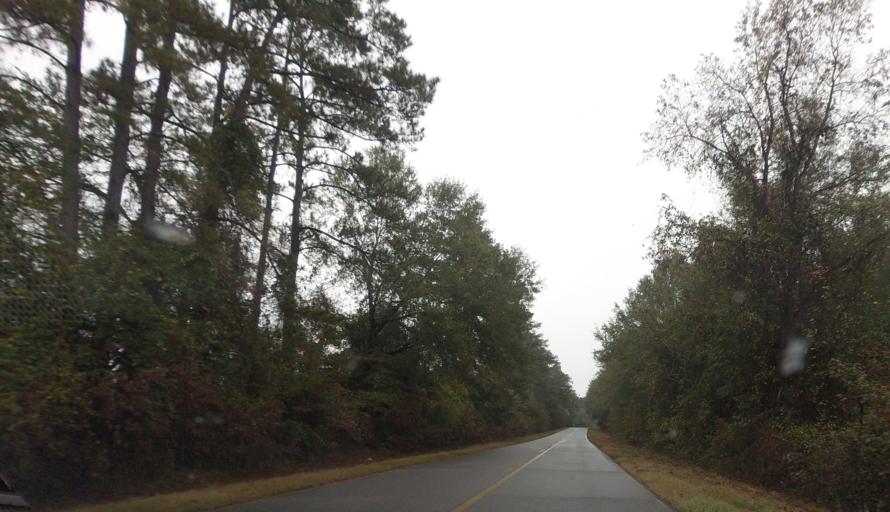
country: US
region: Georgia
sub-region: Macon County
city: Marshallville
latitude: 32.5276
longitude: -83.9822
